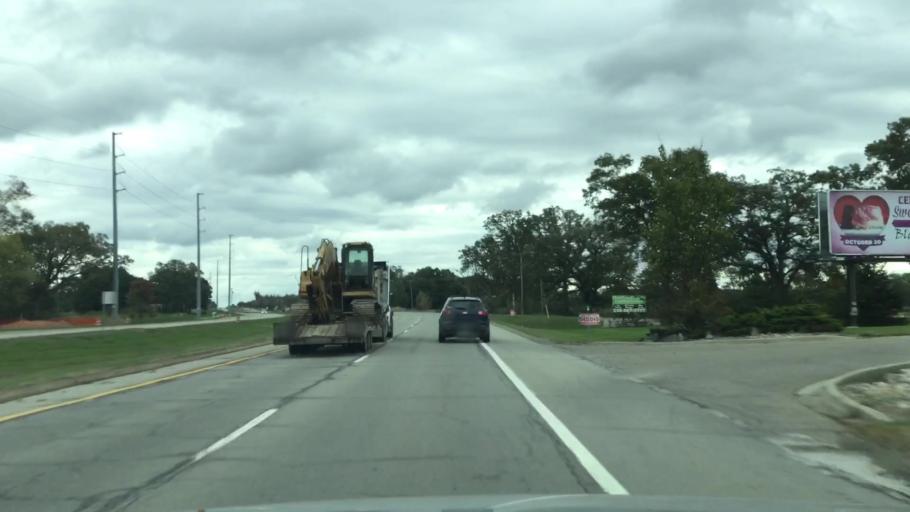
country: US
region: Michigan
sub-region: Oakland County
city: Milford
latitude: 42.6347
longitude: -83.7107
